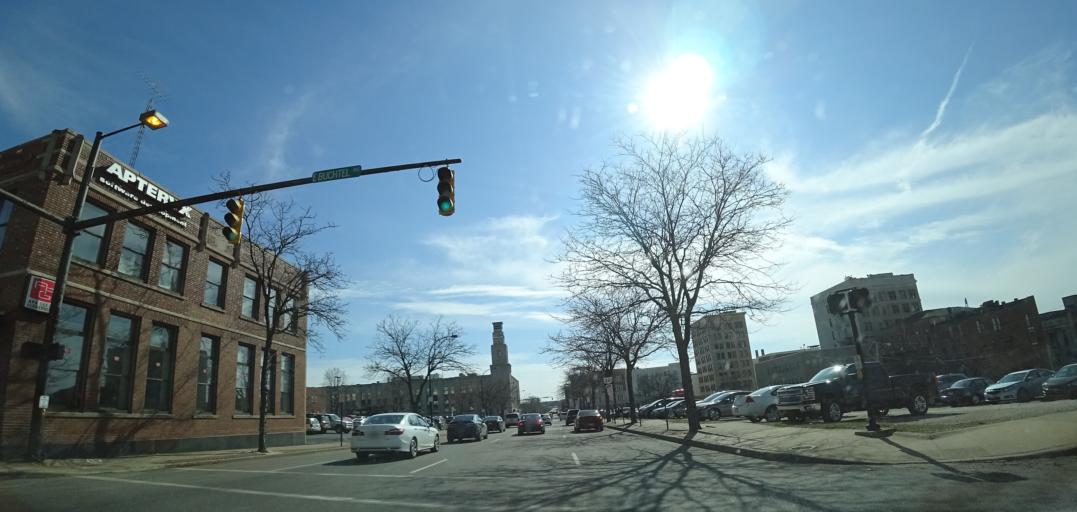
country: US
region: Ohio
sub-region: Summit County
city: Akron
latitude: 41.0772
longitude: -81.5202
